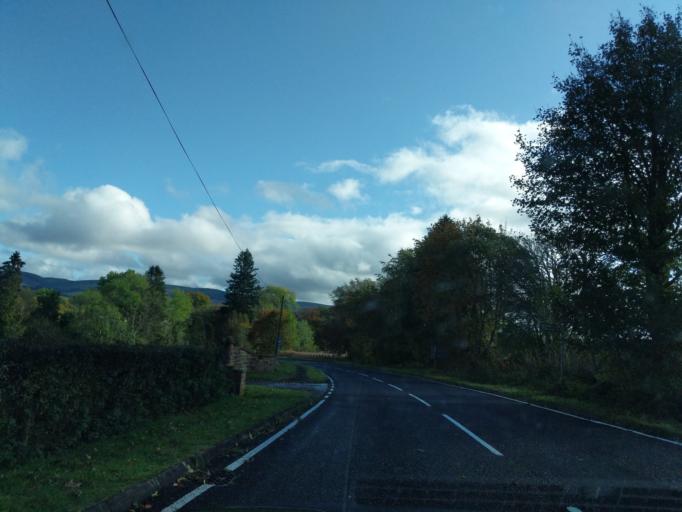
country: GB
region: Scotland
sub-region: Dumfries and Galloway
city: Moffat
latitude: 55.3381
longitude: -3.4560
